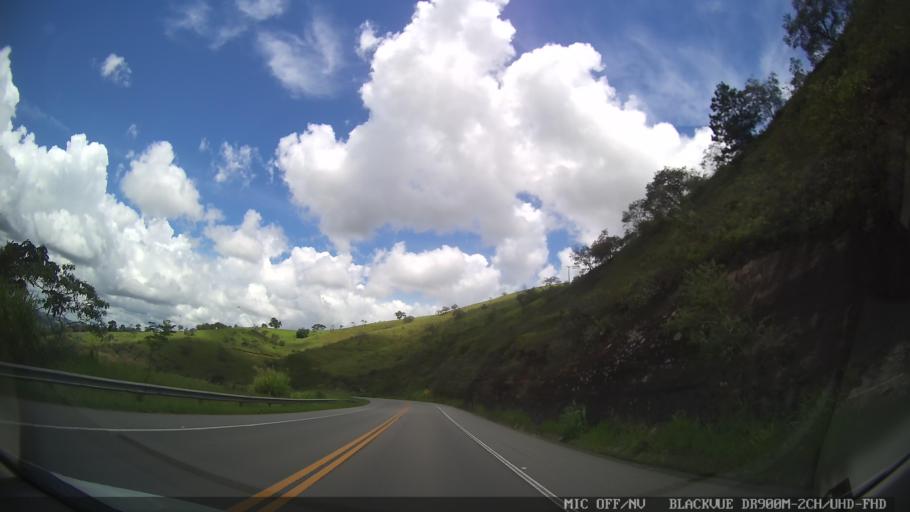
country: BR
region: Sao Paulo
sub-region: Amparo
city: Amparo
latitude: -22.7919
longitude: -46.7180
